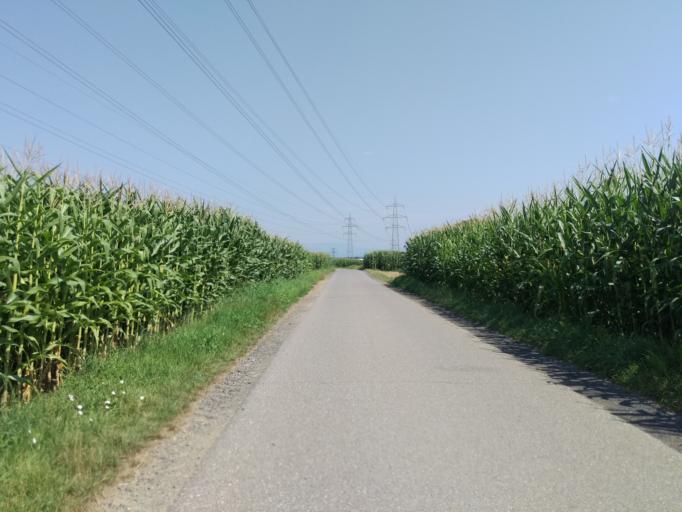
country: AT
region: Styria
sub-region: Politischer Bezirk Graz-Umgebung
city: Werndorf
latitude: 46.9335
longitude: 15.4894
